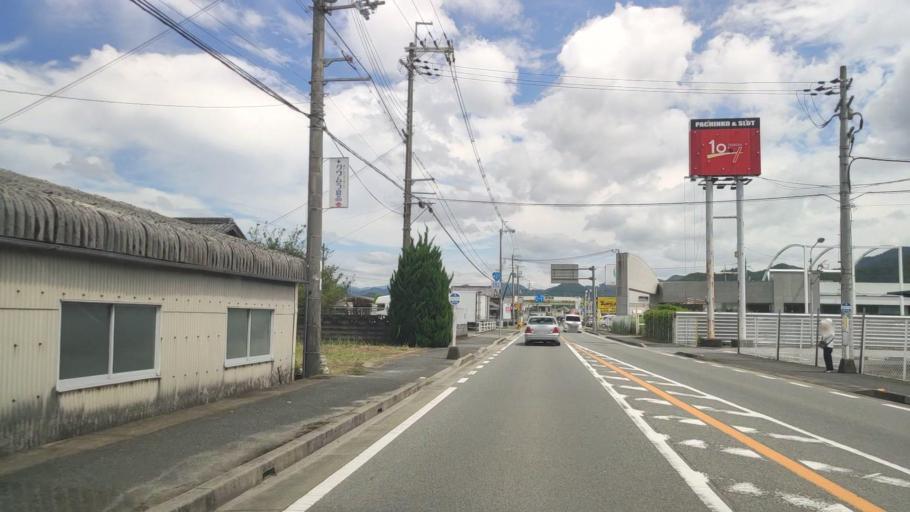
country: JP
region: Hyogo
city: Nishiwaki
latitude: 35.0123
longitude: 134.9613
